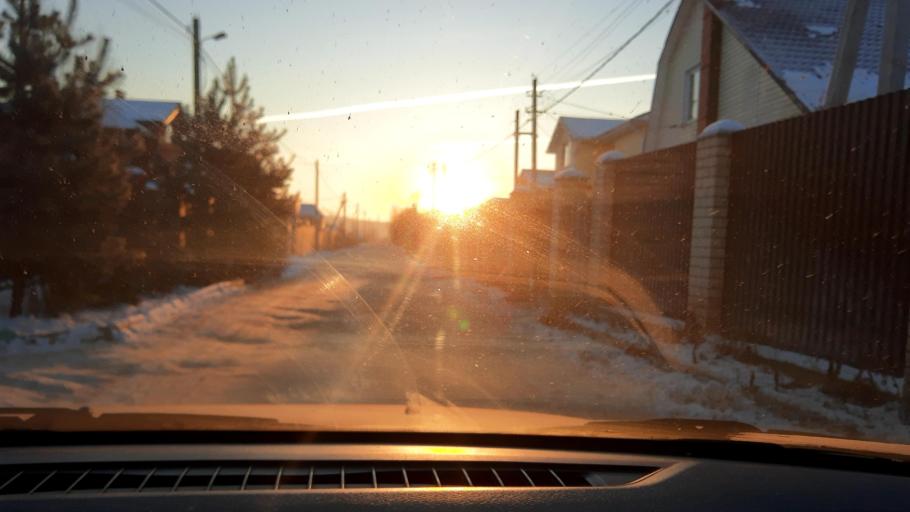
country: RU
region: Nizjnij Novgorod
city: Afonino
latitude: 56.2667
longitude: 44.0639
